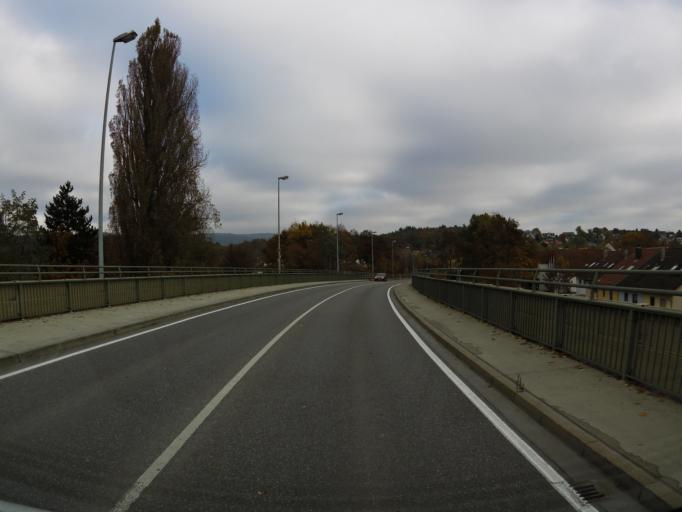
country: DE
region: Baden-Wuerttemberg
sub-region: Freiburg Region
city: Radolfzell am Bodensee
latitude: 47.7489
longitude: 8.9737
